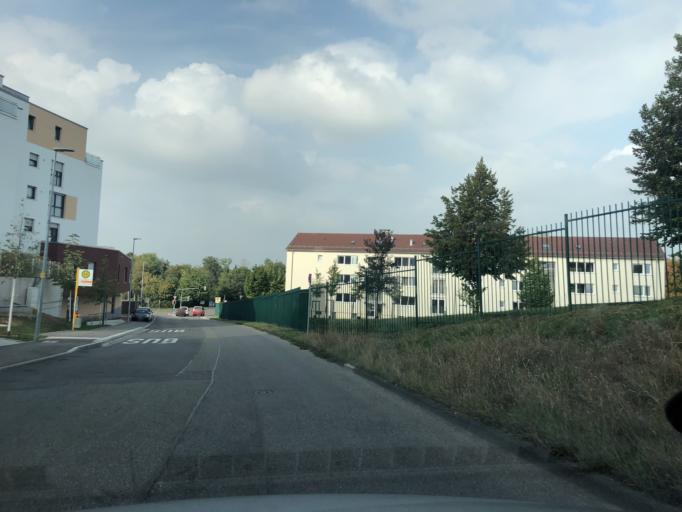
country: DE
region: Baden-Wuerttemberg
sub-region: Regierungsbezirk Stuttgart
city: Kornwestheim
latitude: 48.8263
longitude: 9.1912
